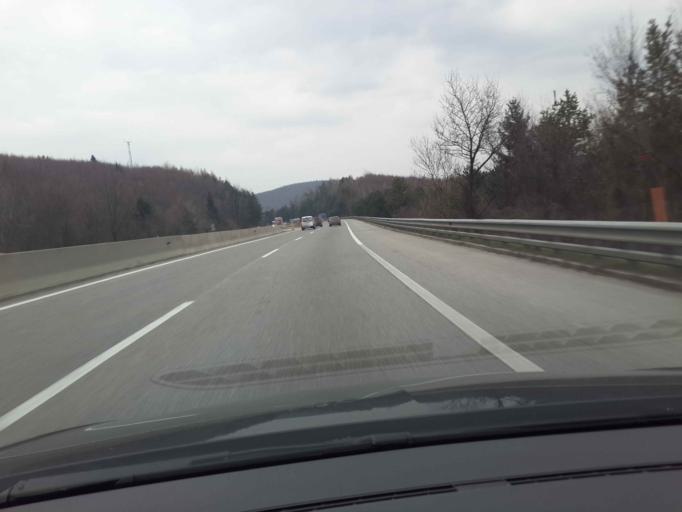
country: AT
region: Lower Austria
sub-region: Politischer Bezirk Baden
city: Klausen-Leopoldsdorf
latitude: 48.1025
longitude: 15.9804
